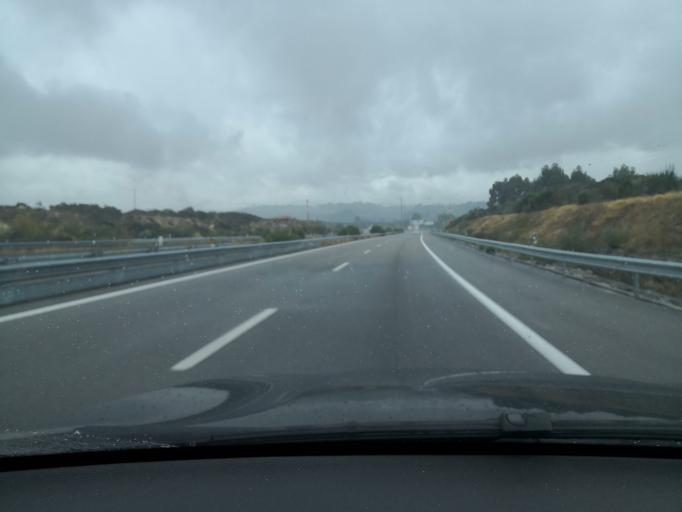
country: PT
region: Porto
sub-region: Pacos de Ferreira
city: Frazao
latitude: 41.2551
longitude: -8.4149
